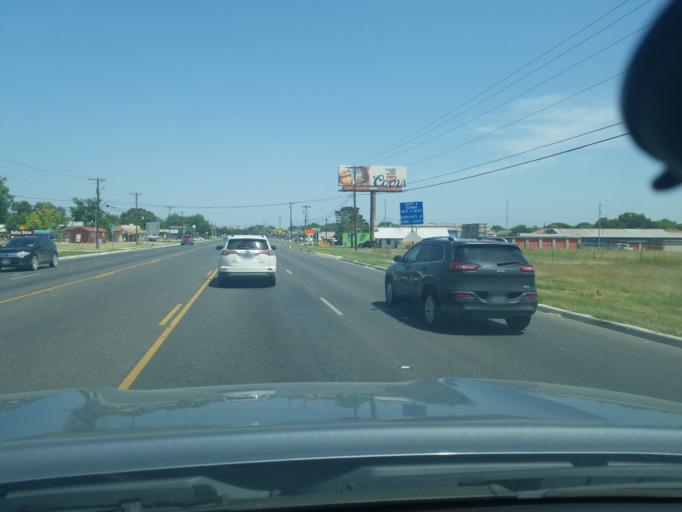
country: US
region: Texas
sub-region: Guadalupe County
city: Lake Dunlap
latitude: 29.6961
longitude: -98.0881
